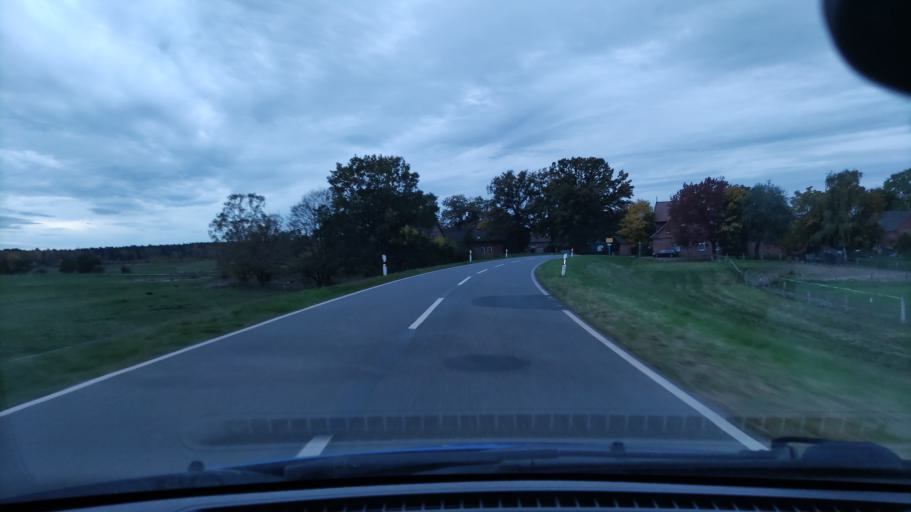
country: DE
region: Lower Saxony
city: Gorleben
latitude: 53.0499
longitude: 11.3905
